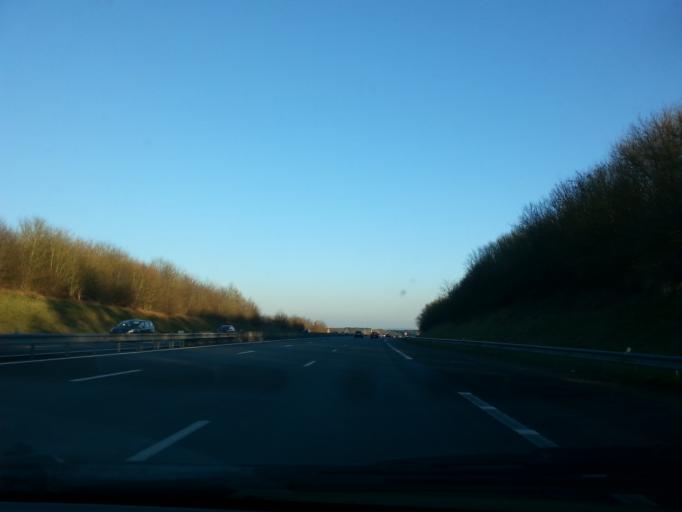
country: FR
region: Pays de la Loire
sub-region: Departement de la Sarthe
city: Lombron
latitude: 48.0745
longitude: 0.4505
